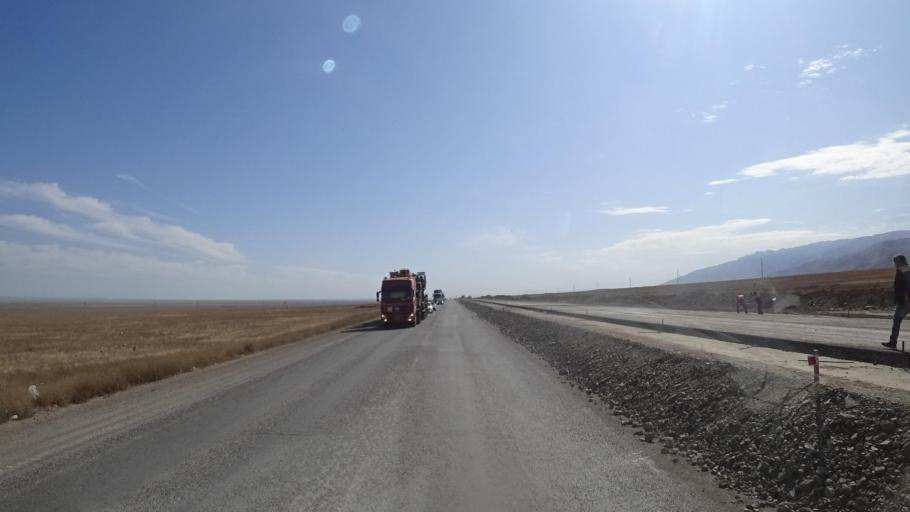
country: KG
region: Chuy
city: Ivanovka
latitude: 43.3834
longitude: 75.1828
